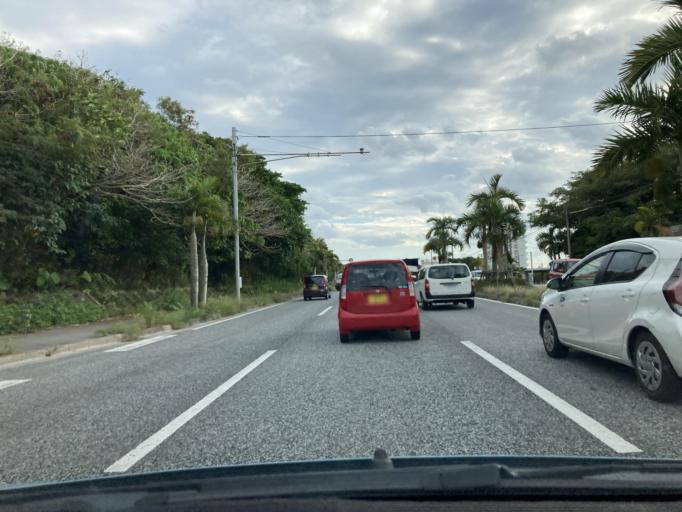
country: JP
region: Okinawa
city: Chatan
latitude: 26.3357
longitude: 127.7516
